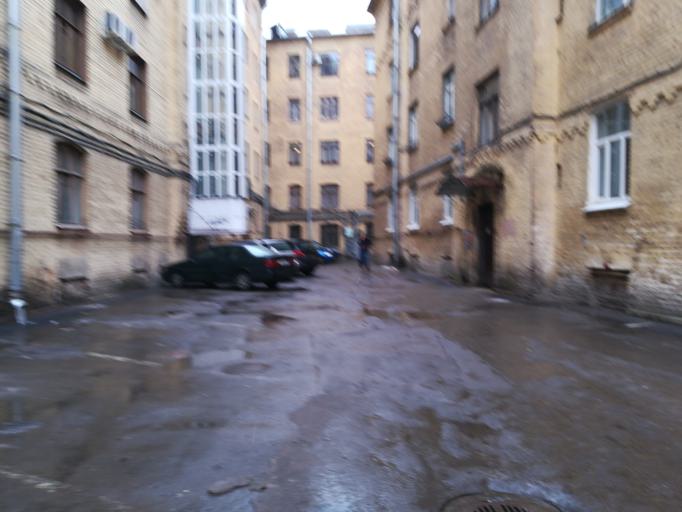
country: RU
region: St.-Petersburg
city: Petrogradka
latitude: 59.9577
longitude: 30.3307
